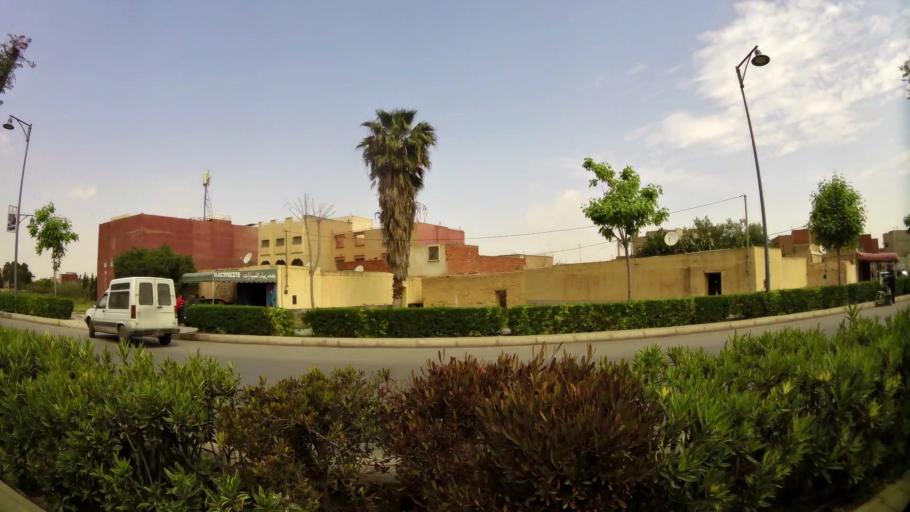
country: MA
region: Oriental
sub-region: Oujda-Angad
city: Oujda
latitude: 34.6794
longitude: -1.8934
